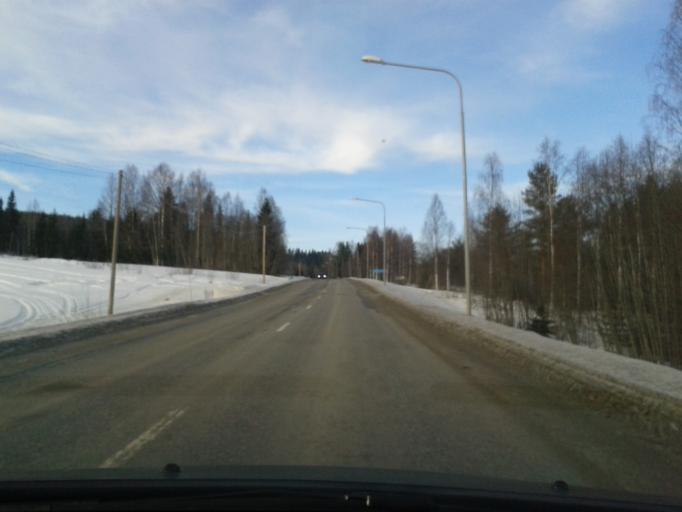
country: SE
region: Vaesternorrland
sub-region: OErnskoeldsviks Kommun
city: Bredbyn
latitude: 63.4876
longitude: 18.0847
